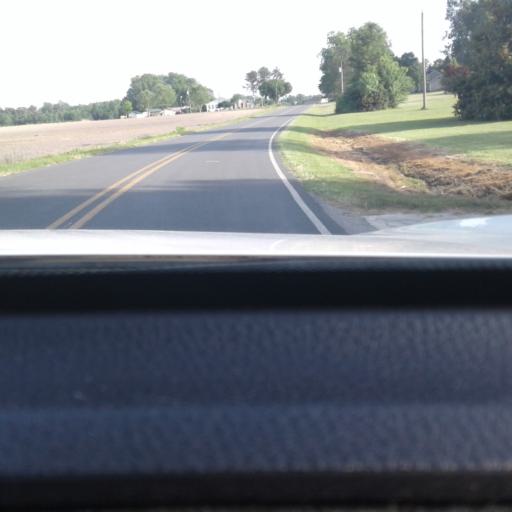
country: US
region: North Carolina
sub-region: Harnett County
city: Dunn
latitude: 35.3393
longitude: -78.5764
